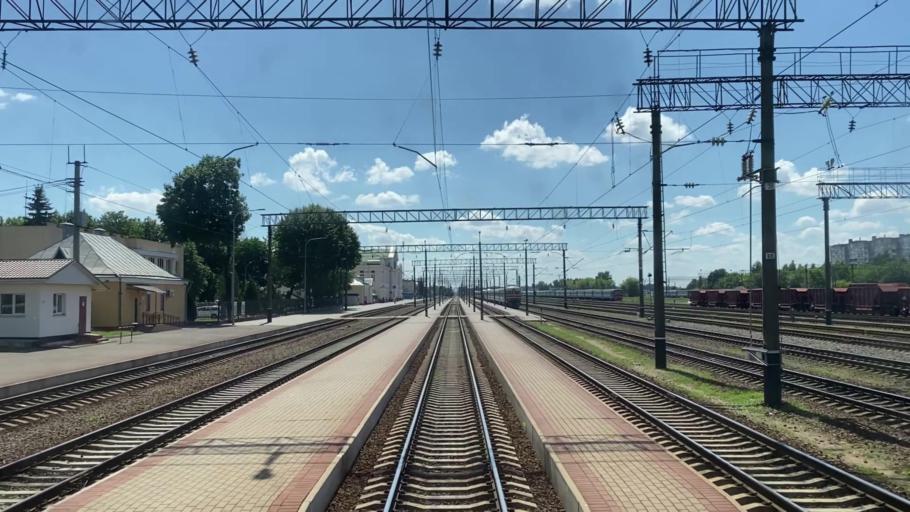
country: BY
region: Brest
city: Baranovichi
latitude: 53.1313
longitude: 26.0399
